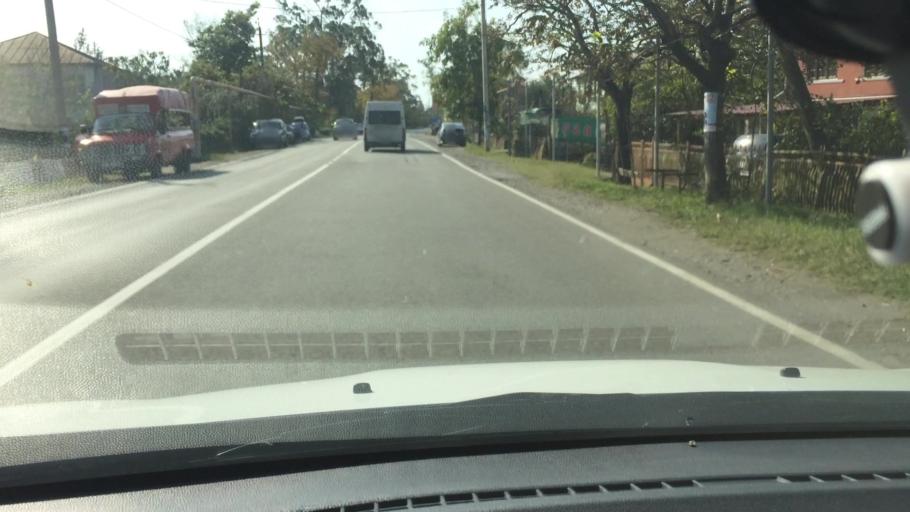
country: GE
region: Guria
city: Urek'i
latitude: 42.0094
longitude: 41.7808
